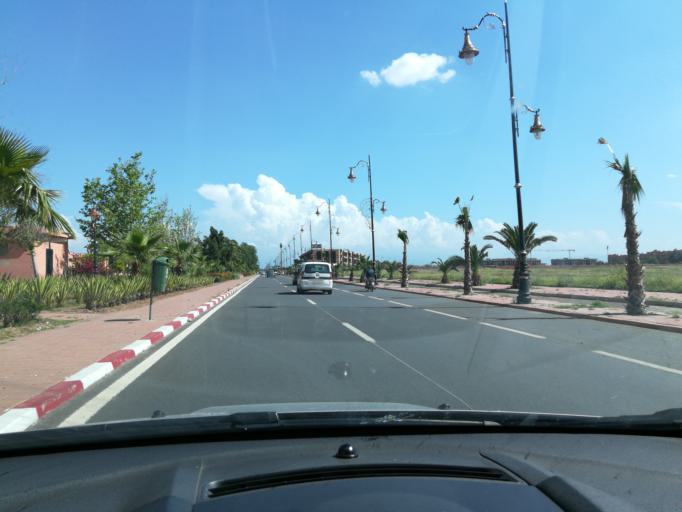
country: MA
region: Marrakech-Tensift-Al Haouz
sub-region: Marrakech
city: Marrakesh
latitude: 31.5898
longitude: -7.9900
